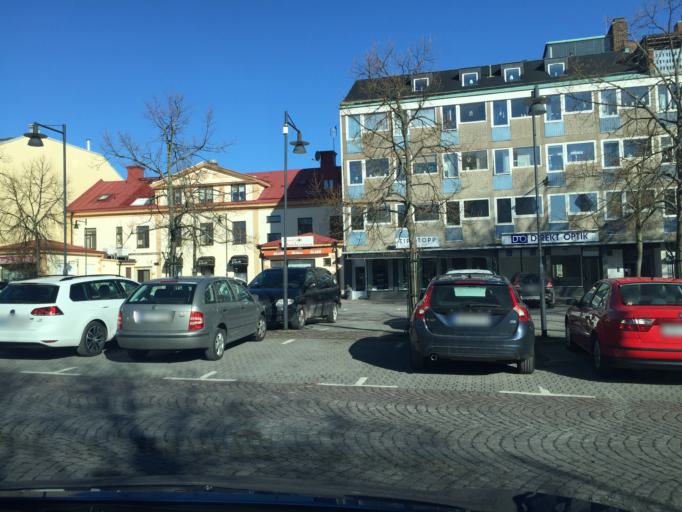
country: SE
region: Kalmar
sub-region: Oskarshamns Kommun
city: Oskarshamn
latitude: 57.2648
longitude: 16.4486
